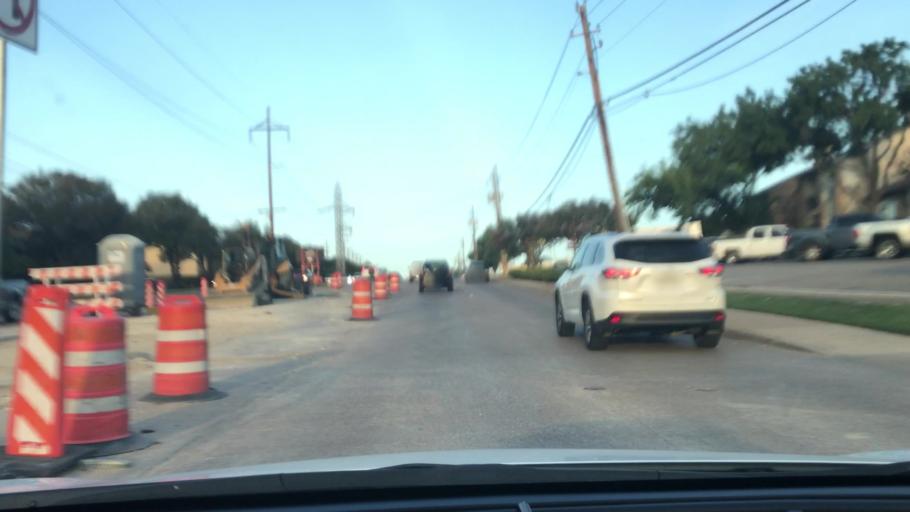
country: US
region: Texas
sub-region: Dallas County
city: Richardson
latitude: 32.9400
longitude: -96.7553
